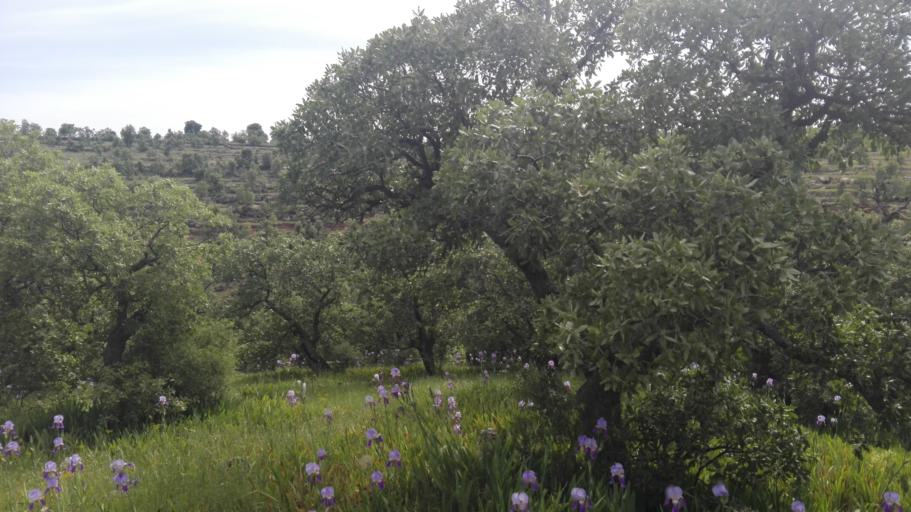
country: TR
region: Mardin
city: Kilavuz
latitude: 37.4778
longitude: 41.7758
